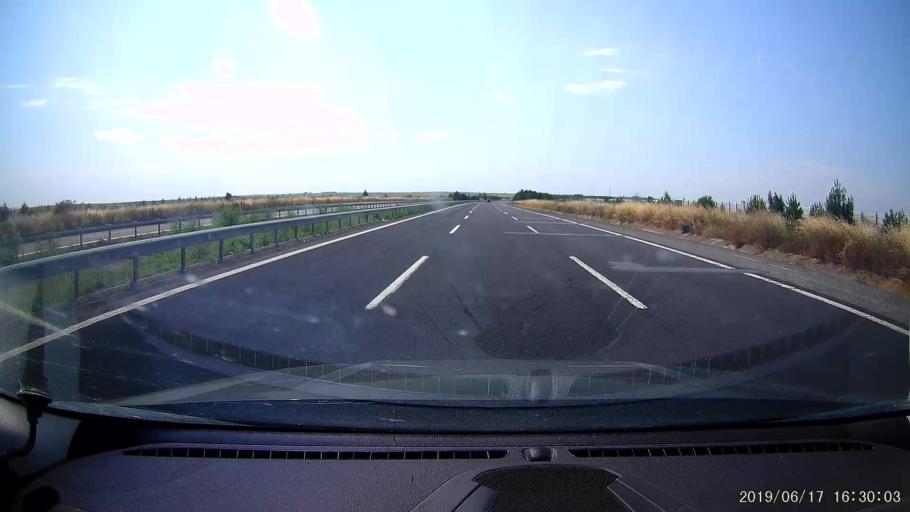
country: TR
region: Tekirdag
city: Beyazkoy
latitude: 41.3417
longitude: 27.6651
